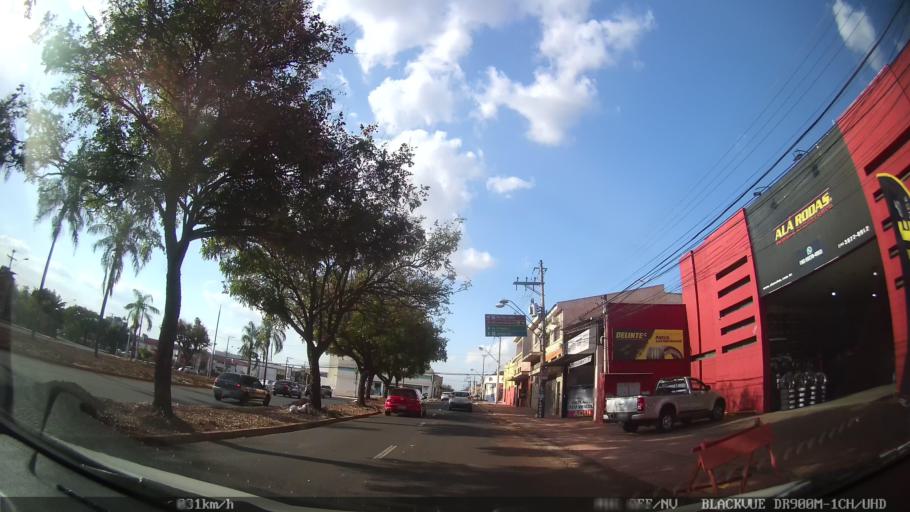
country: BR
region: Sao Paulo
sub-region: Ribeirao Preto
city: Ribeirao Preto
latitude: -21.1633
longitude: -47.8113
